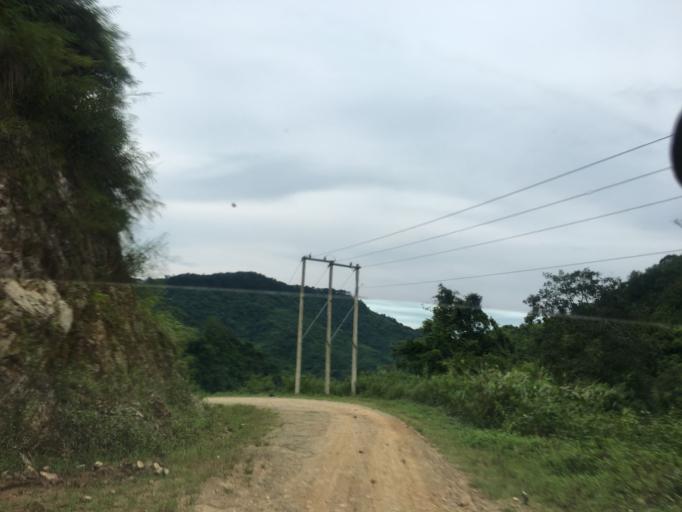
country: LA
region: Xiangkhoang
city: Phonsavan
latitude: 19.7109
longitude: 103.0700
